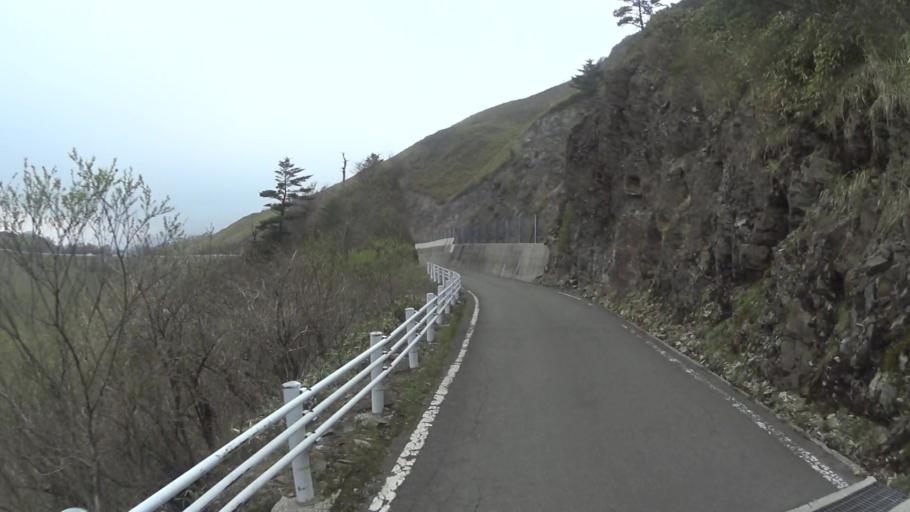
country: JP
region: Ehime
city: Saijo
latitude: 33.7830
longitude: 133.2329
